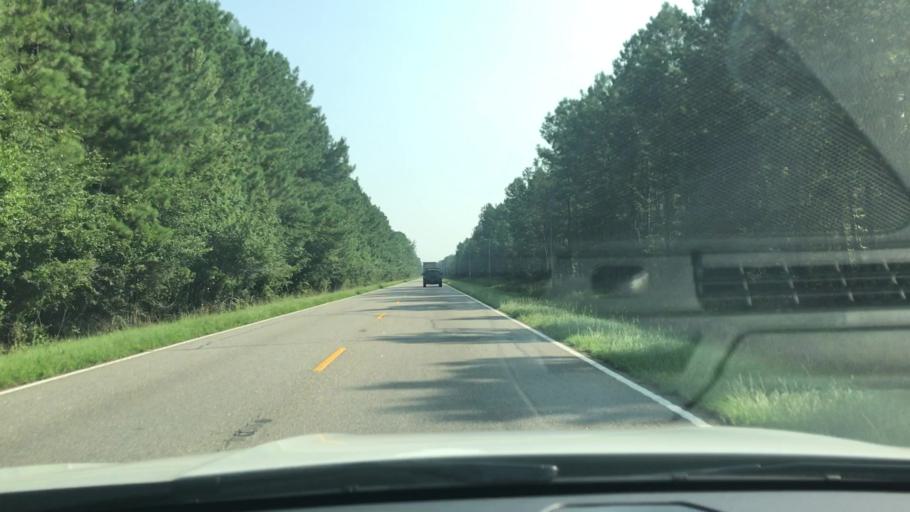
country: US
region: South Carolina
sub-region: Georgetown County
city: Georgetown
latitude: 33.4982
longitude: -79.2602
